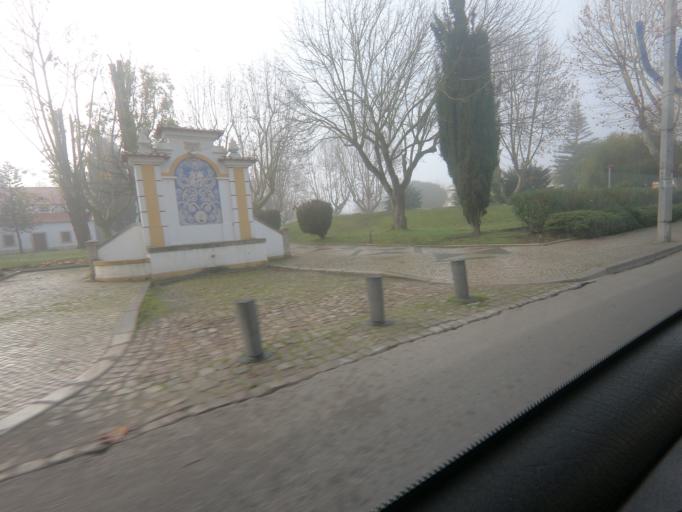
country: PT
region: Setubal
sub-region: Palmela
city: Pinhal Novo
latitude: 38.6314
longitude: -8.9157
